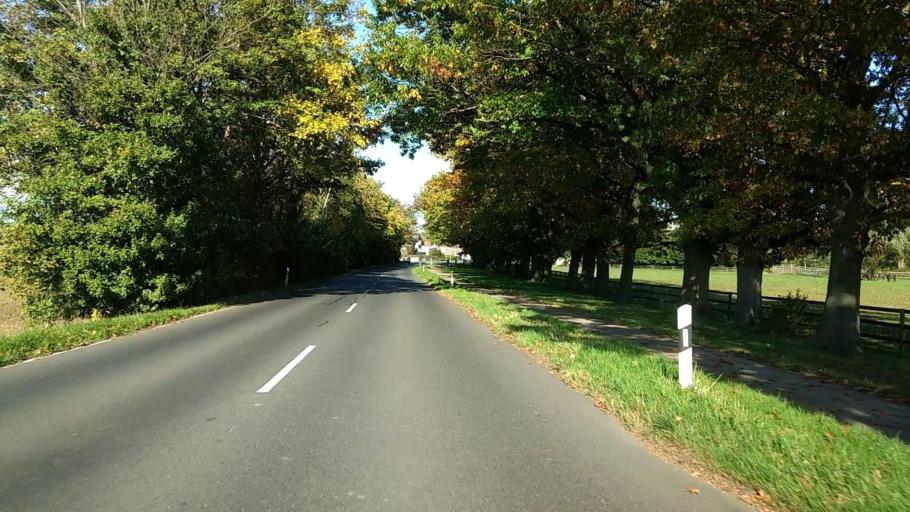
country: DE
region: North Rhine-Westphalia
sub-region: Regierungsbezirk Koln
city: Bergheim
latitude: 50.9273
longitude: 6.6838
